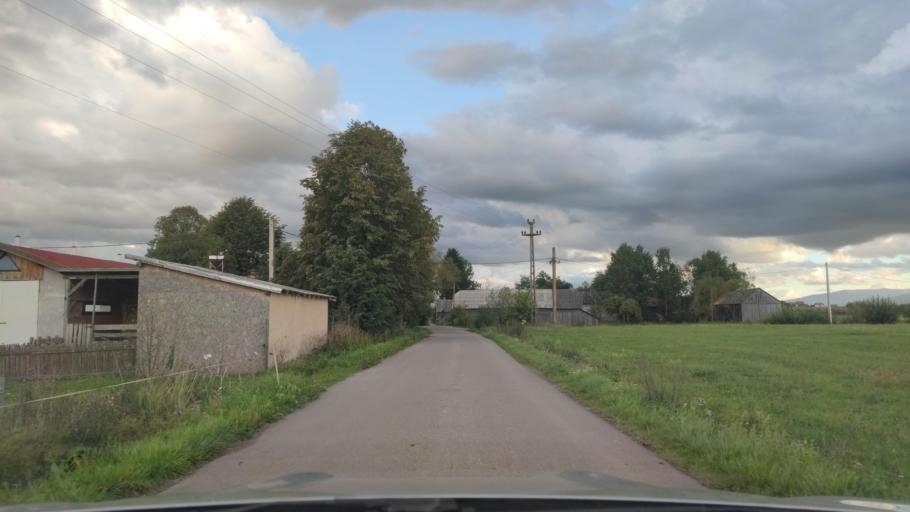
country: RO
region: Harghita
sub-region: Comuna Remetea
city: Remetea
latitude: 46.8117
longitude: 25.4360
